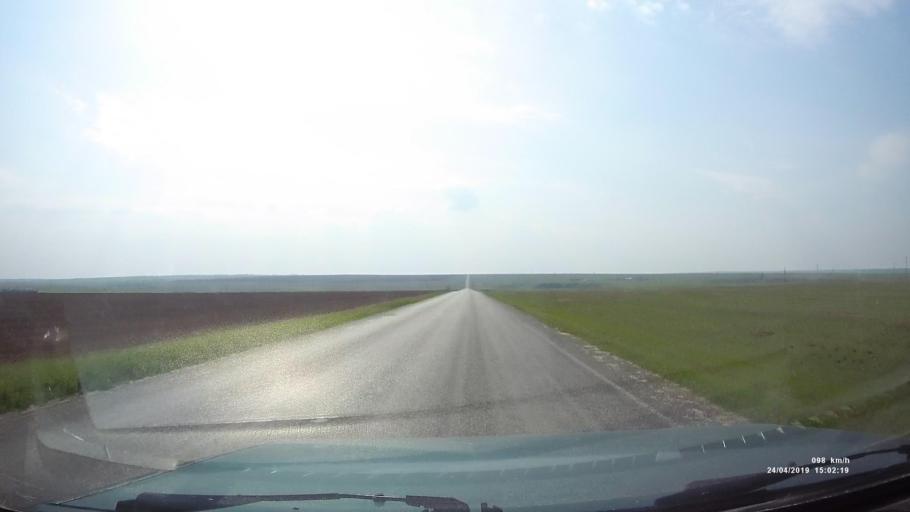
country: RU
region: Rostov
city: Remontnoye
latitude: 46.5662
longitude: 43.5146
